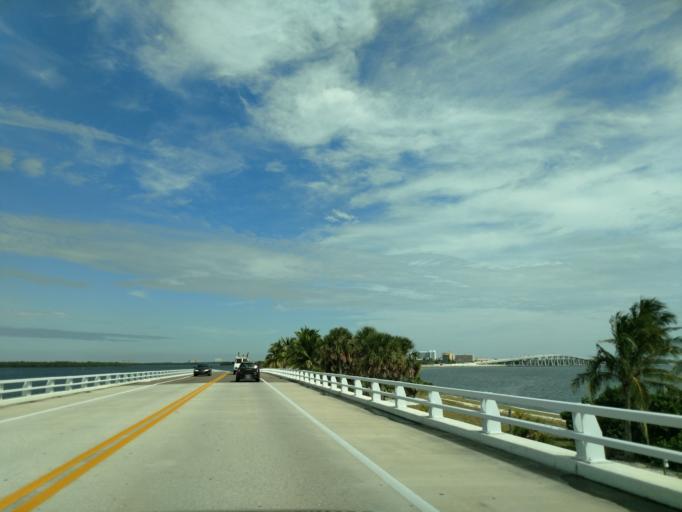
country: US
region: Florida
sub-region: Lee County
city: Punta Rassa
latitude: 26.4760
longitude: -82.0260
